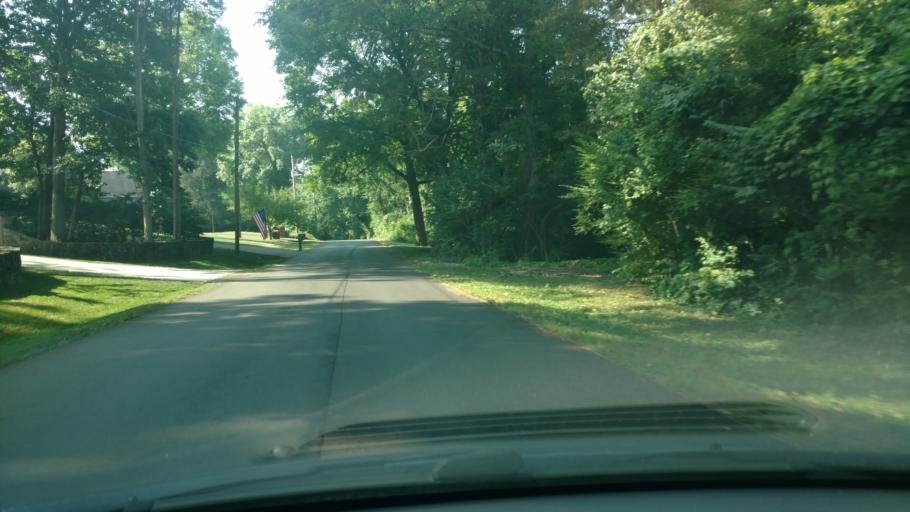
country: US
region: Tennessee
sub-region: Davidson County
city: Lakewood
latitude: 36.2206
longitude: -86.7092
